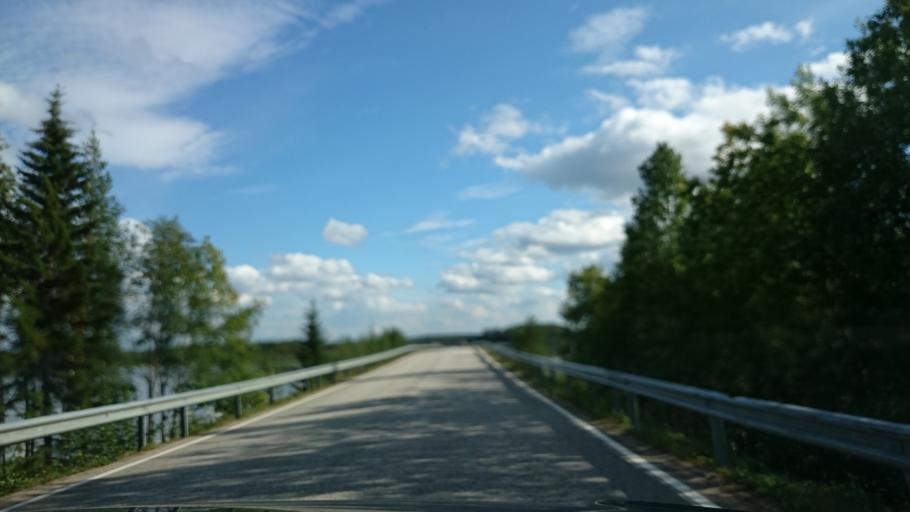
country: FI
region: Kainuu
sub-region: Kehys-Kainuu
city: Suomussalmi
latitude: 64.7647
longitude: 29.3707
